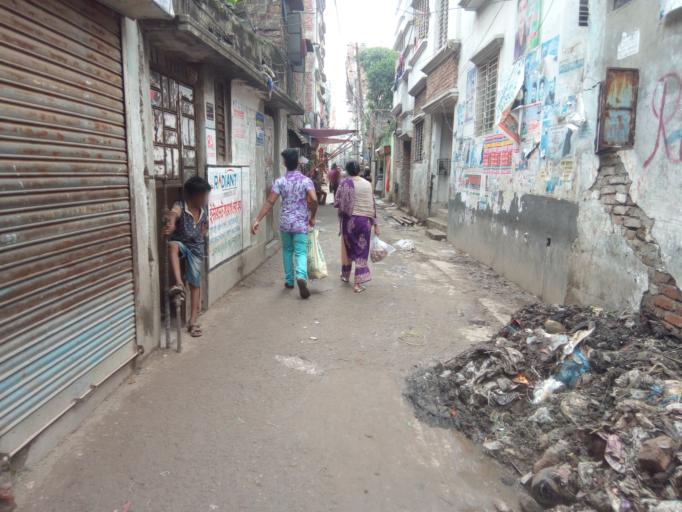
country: BD
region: Dhaka
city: Azimpur
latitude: 23.7159
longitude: 90.3822
